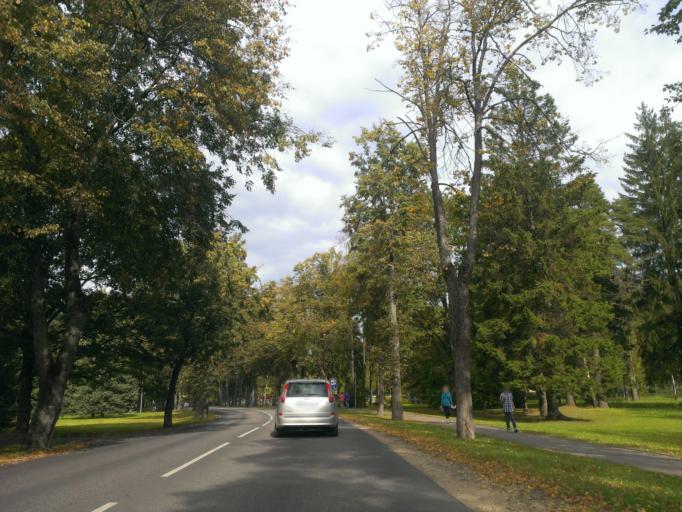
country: LV
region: Sigulda
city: Sigulda
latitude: 57.1560
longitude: 24.8545
